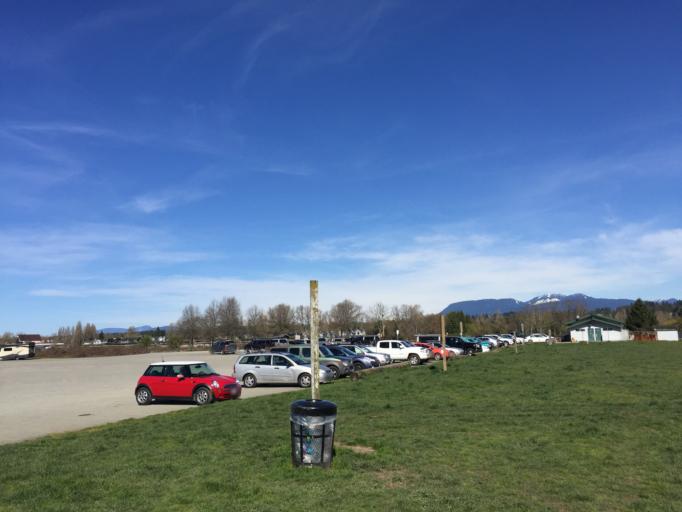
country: CA
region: British Columbia
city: Richmond
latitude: 49.2124
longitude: -123.1685
